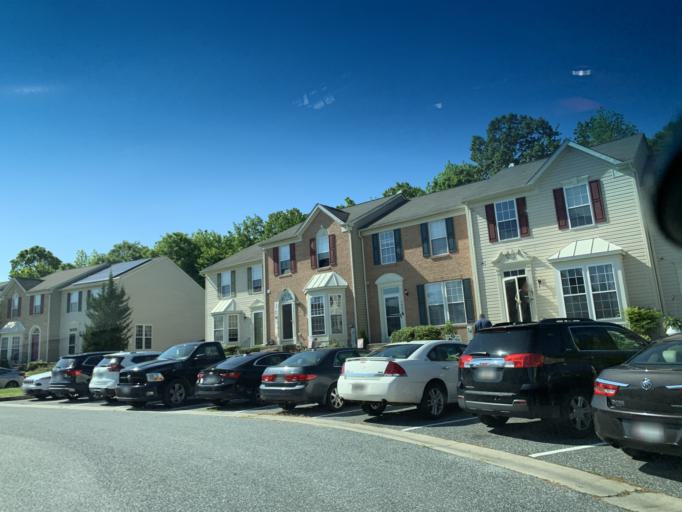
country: US
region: Maryland
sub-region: Harford County
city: Perryman
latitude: 39.4948
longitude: -76.2158
